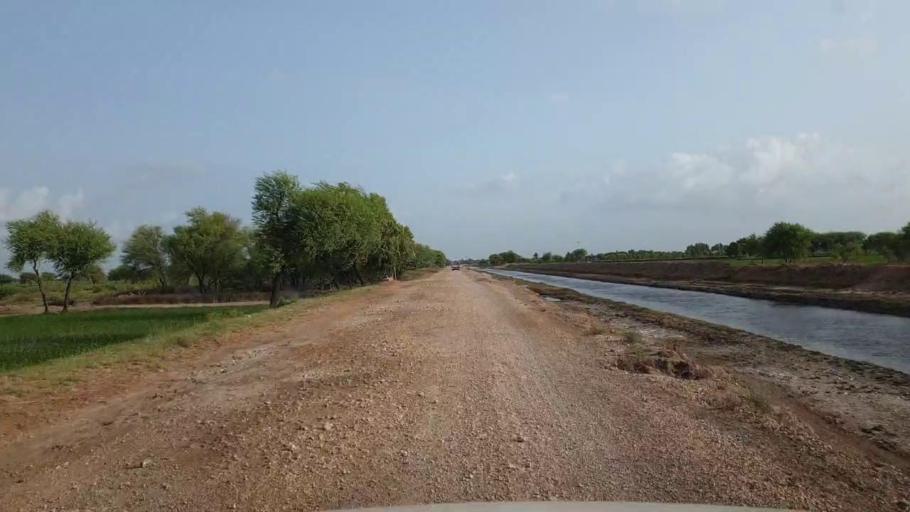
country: PK
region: Sindh
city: Kario
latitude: 24.8526
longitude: 68.6521
